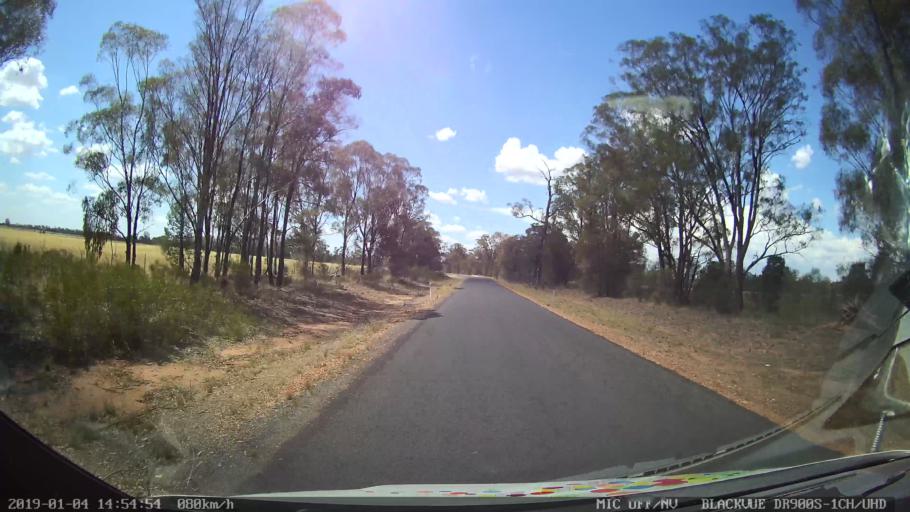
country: AU
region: New South Wales
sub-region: Dubbo Municipality
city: Dubbo
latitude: -31.9852
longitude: 148.6549
